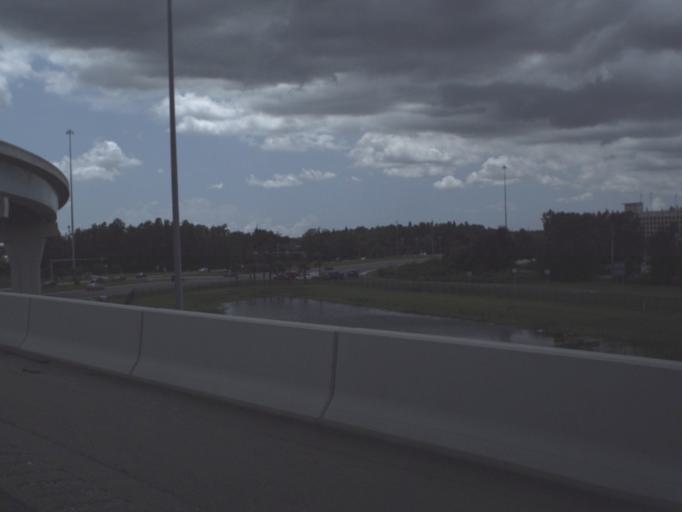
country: US
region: Florida
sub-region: Hillsborough County
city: Pebble Creek
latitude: 28.1232
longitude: -82.3749
